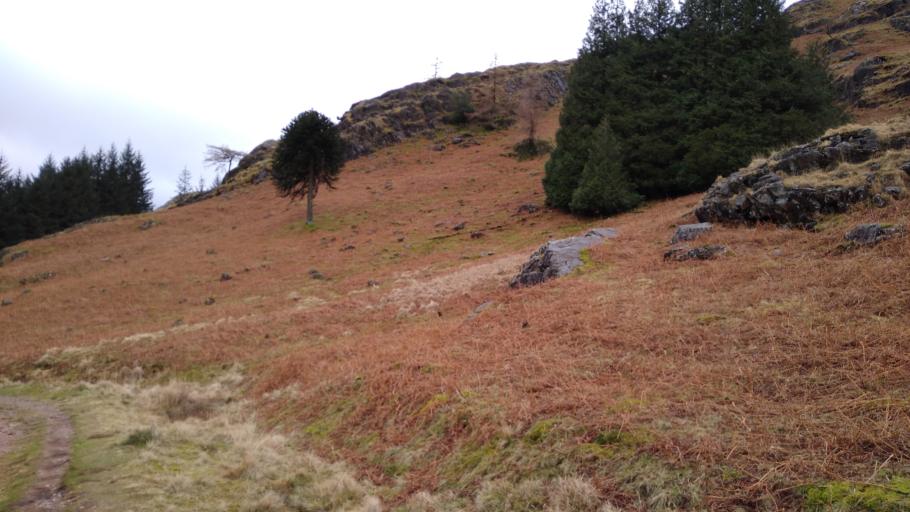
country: GB
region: England
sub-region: Cumbria
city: Ambleside
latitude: 54.4317
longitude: -3.0944
